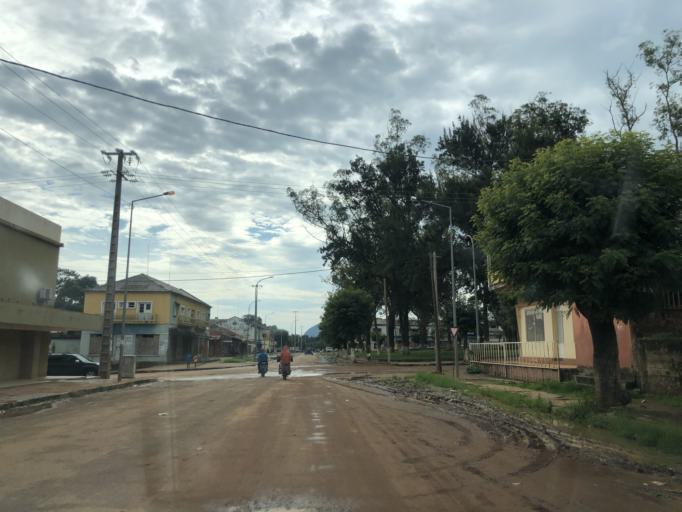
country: AO
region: Cuanza Sul
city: Uacu Cungo
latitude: -11.3643
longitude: 15.1173
